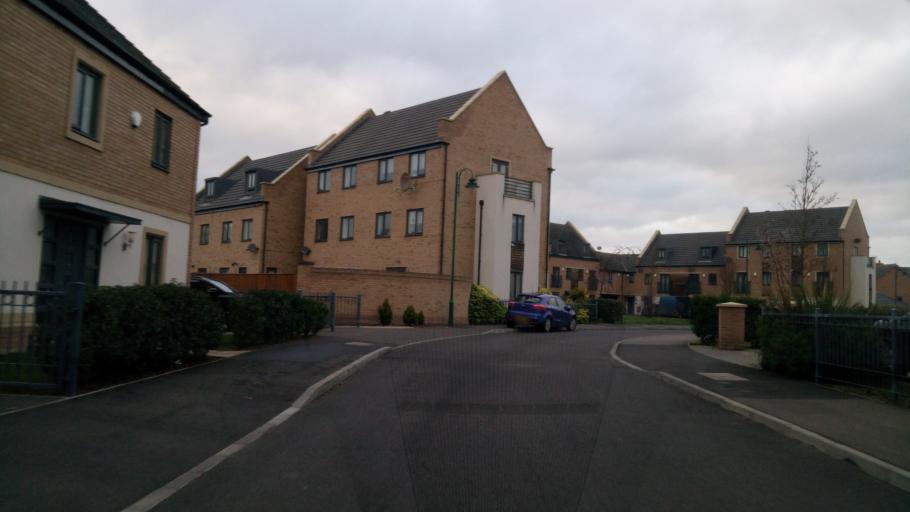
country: GB
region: England
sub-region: Cambridgeshire
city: Yaxley
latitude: 52.5303
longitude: -0.2830
